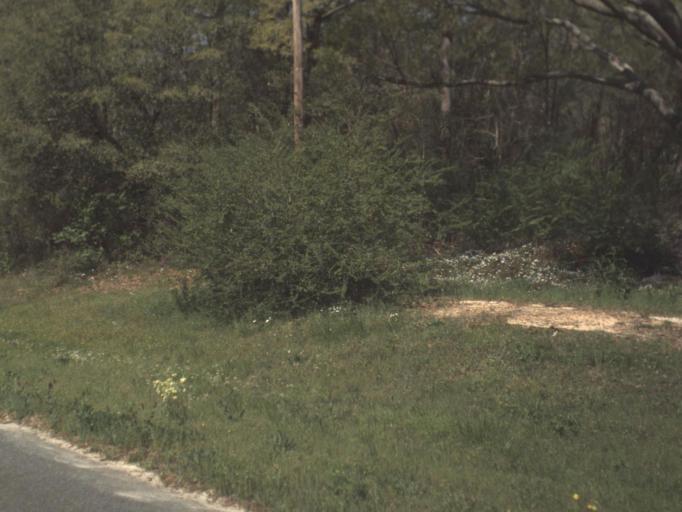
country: US
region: Florida
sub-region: Jackson County
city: Graceville
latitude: 30.9018
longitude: -85.4493
